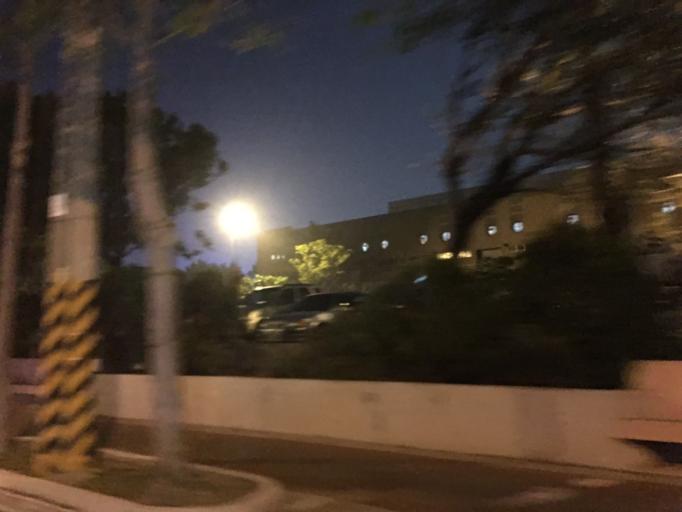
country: TW
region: Taiwan
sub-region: Miaoli
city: Miaoli
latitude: 24.6897
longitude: 120.8856
